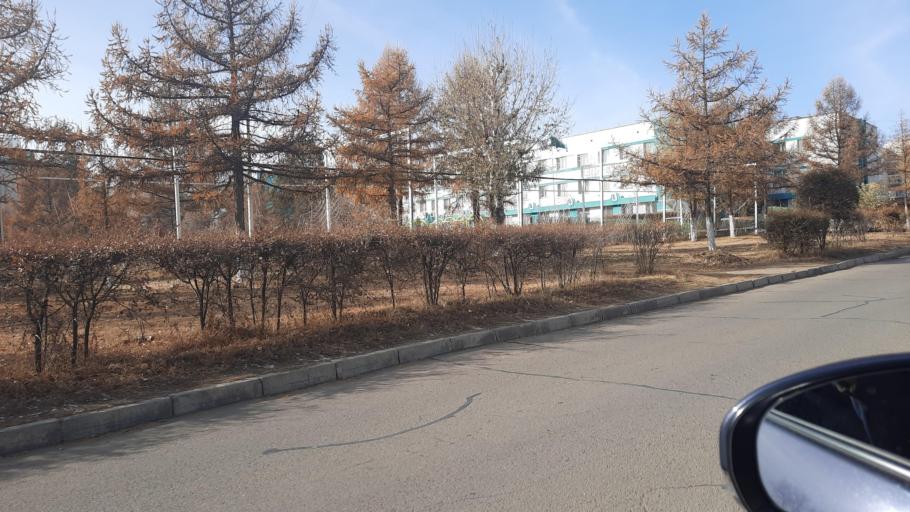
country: MN
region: Orhon
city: Erdenet
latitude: 49.0313
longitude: 104.0548
